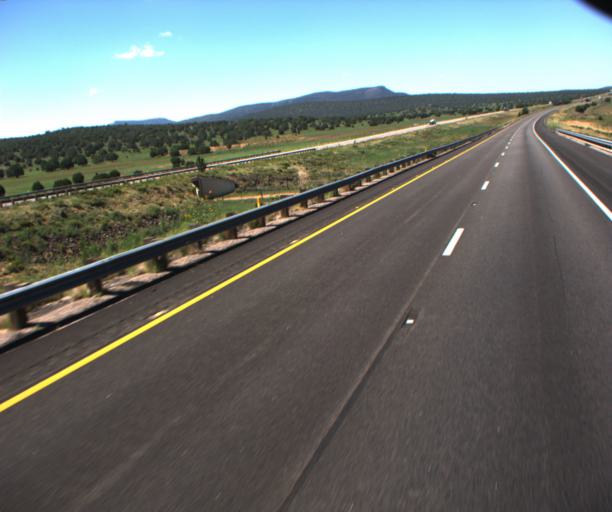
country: US
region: Arizona
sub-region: Mohave County
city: Peach Springs
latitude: 35.2367
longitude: -113.2080
